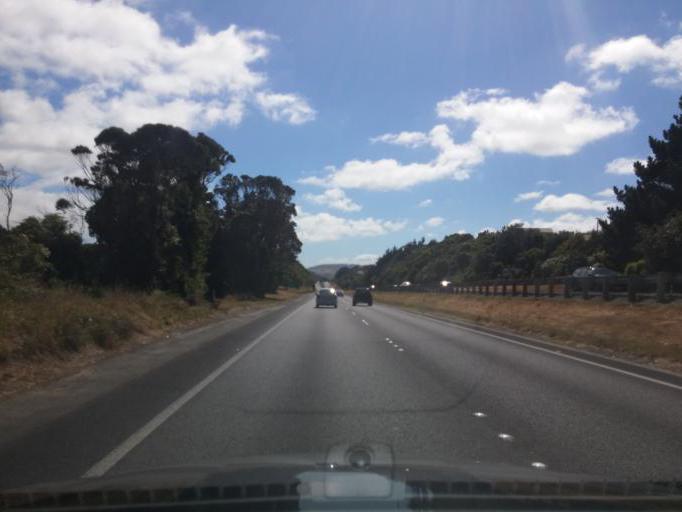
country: NZ
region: Wellington
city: Petone
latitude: -41.2153
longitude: 174.8127
